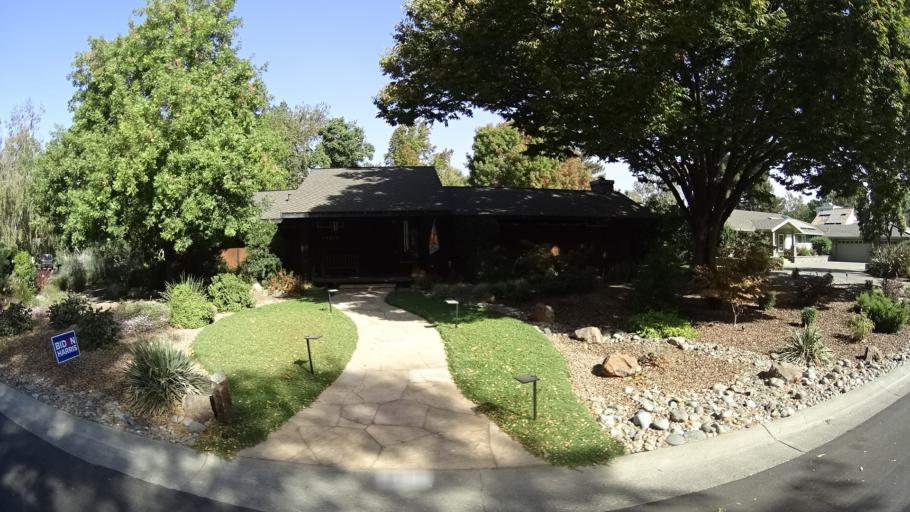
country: US
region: California
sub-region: Yolo County
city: Davis
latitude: 38.5459
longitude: -121.6820
